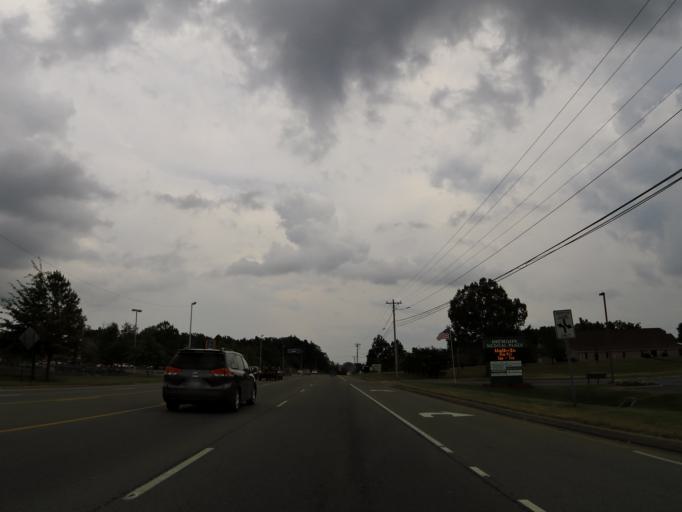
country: US
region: Tennessee
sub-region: Dickson County
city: Dickson
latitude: 36.0502
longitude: -87.3645
